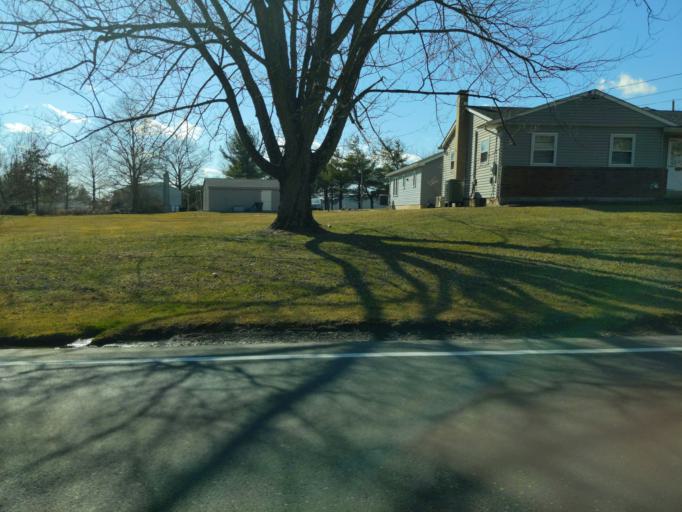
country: US
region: Pennsylvania
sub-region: Montgomery County
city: Pennsburg
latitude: 40.3979
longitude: -75.4702
